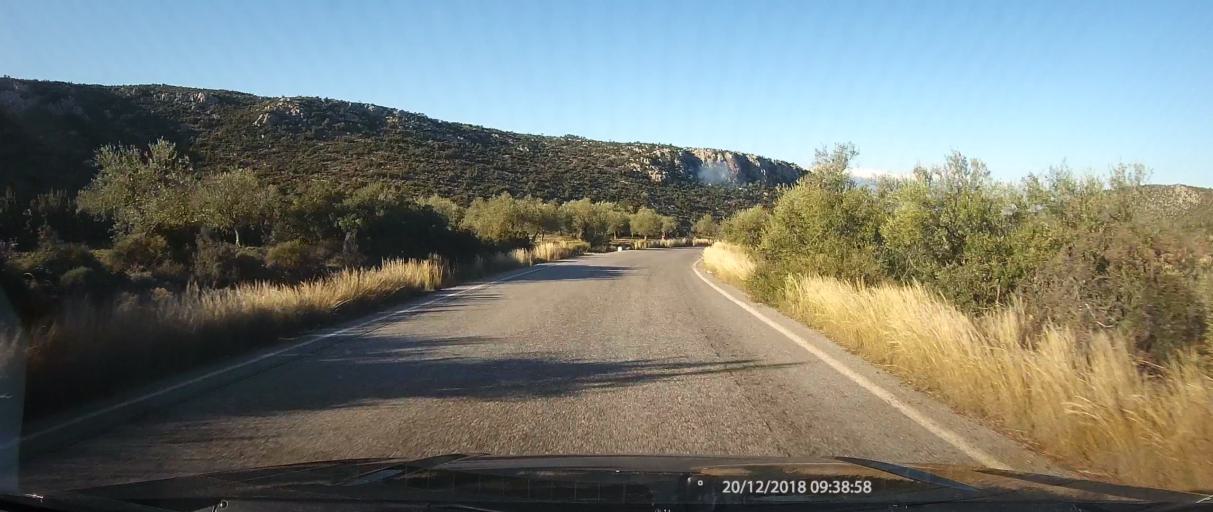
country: GR
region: Peloponnese
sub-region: Nomos Lakonias
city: Yerakion
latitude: 36.9387
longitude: 22.7831
